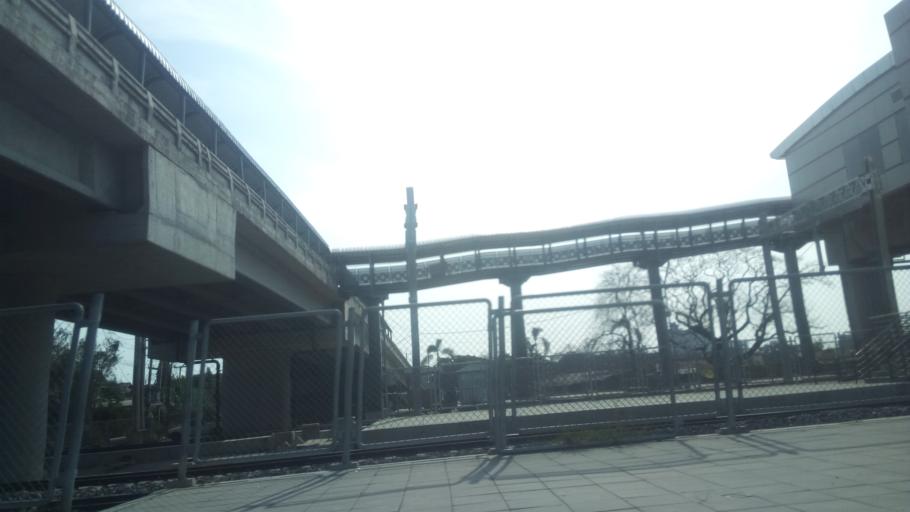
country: TH
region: Bangkok
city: Don Mueang
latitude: 13.9671
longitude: 100.6049
